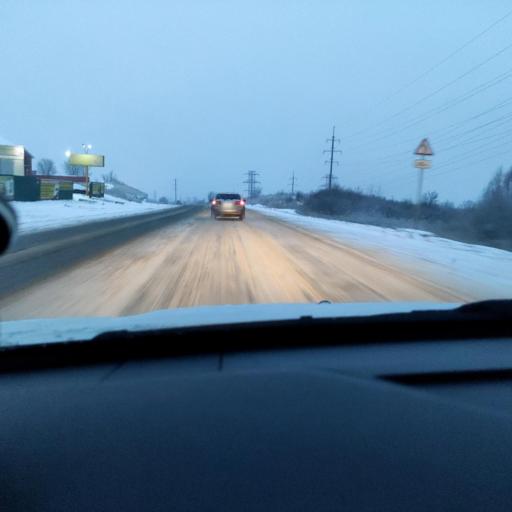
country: RU
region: Samara
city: Smyshlyayevka
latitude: 53.2475
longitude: 50.4748
